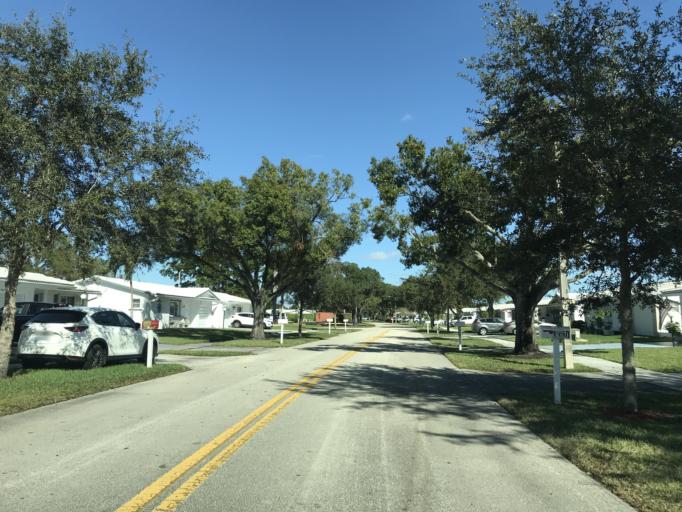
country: US
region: Florida
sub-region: Broward County
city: Plantation
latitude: 26.1396
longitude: -80.2664
